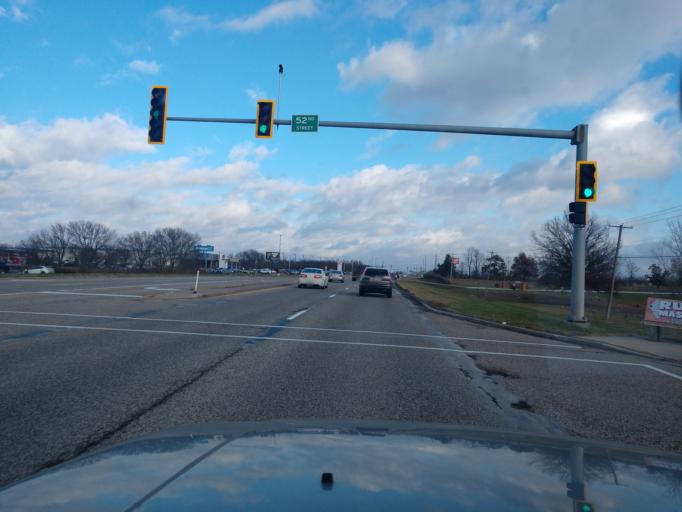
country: US
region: Illinois
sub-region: Adams County
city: Quincy
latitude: 39.9352
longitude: -91.3339
